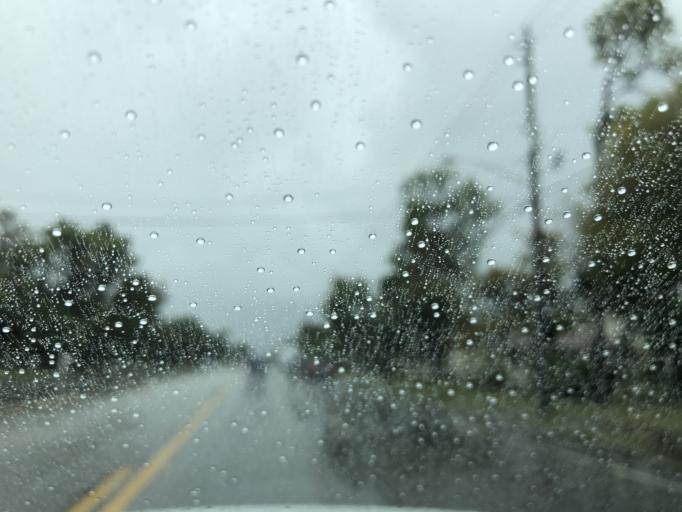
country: US
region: Florida
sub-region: Palm Beach County
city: Haverhill
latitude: 26.6948
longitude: -80.1197
